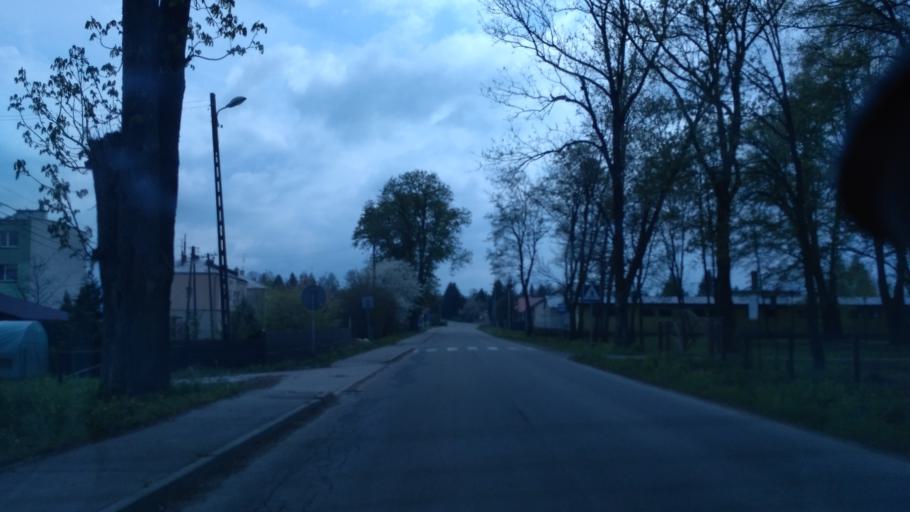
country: PL
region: Subcarpathian Voivodeship
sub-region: Powiat brzozowski
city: Haczow
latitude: 49.6707
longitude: 21.8953
